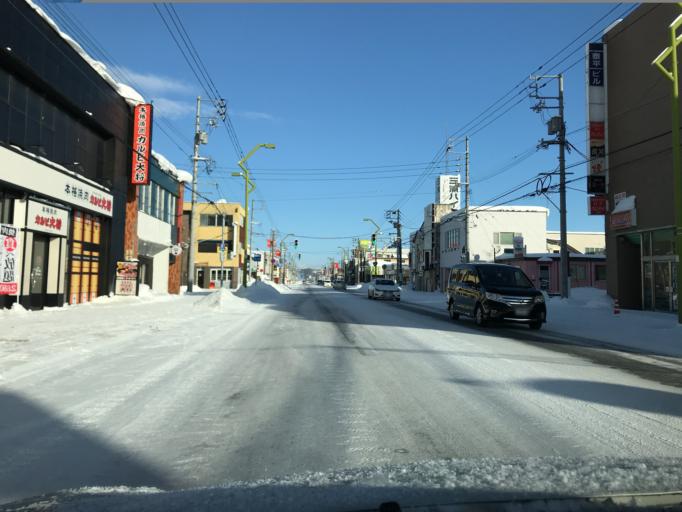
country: JP
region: Hokkaido
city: Nayoro
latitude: 44.3508
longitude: 142.4571
